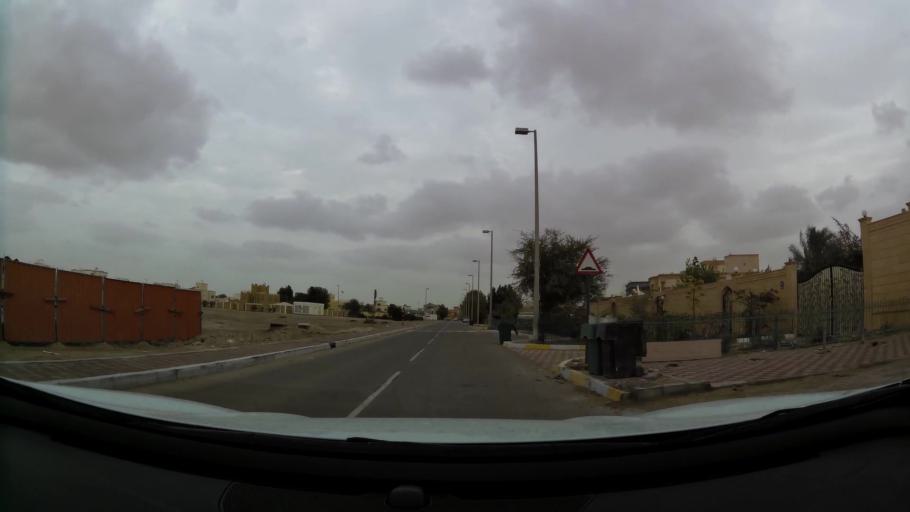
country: AE
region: Abu Dhabi
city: Abu Dhabi
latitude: 24.3833
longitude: 54.6549
